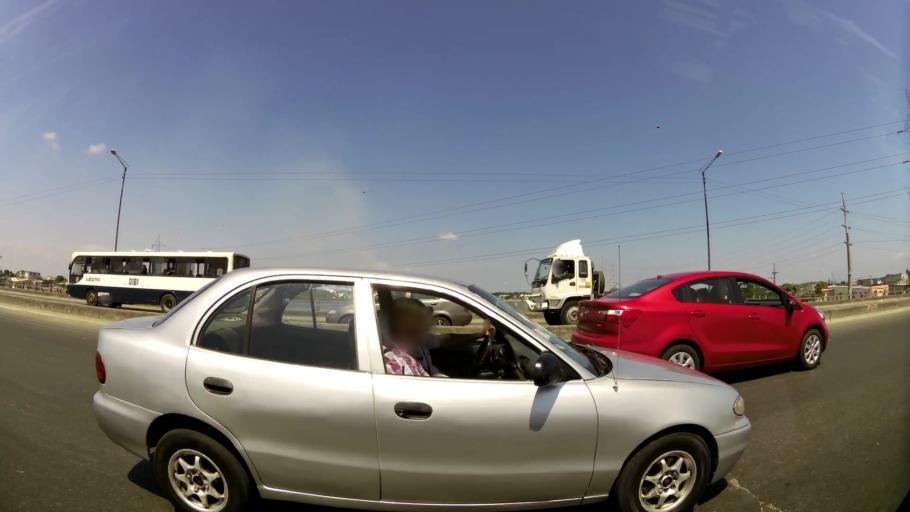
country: EC
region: Guayas
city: Guayaquil
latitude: -2.2392
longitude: -79.9131
